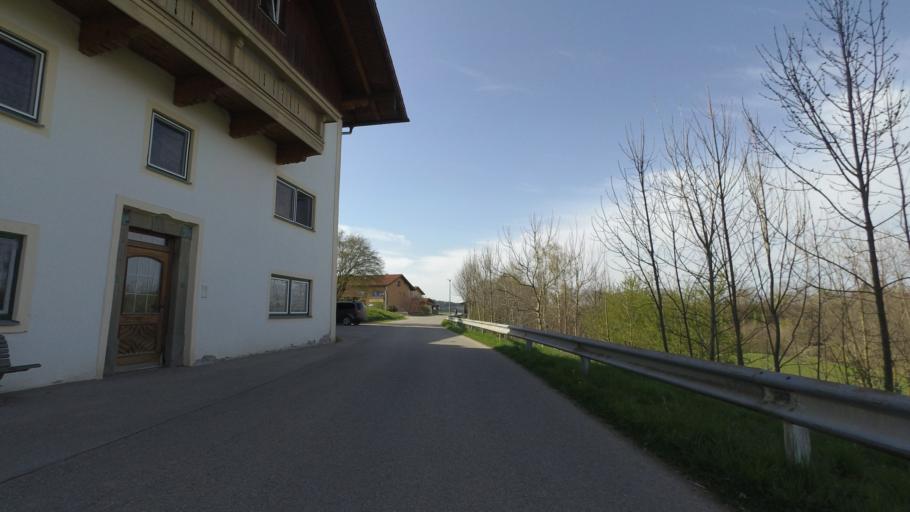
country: DE
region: Bavaria
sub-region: Upper Bavaria
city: Nussdorf
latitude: 47.9100
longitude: 12.6174
